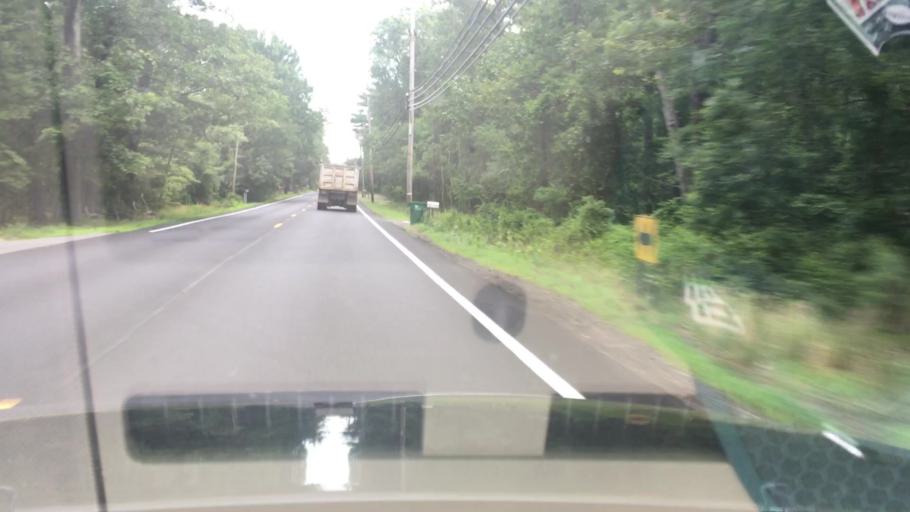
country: US
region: New Jersey
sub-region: Ocean County
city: Vista Center
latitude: 40.0973
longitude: -74.3853
